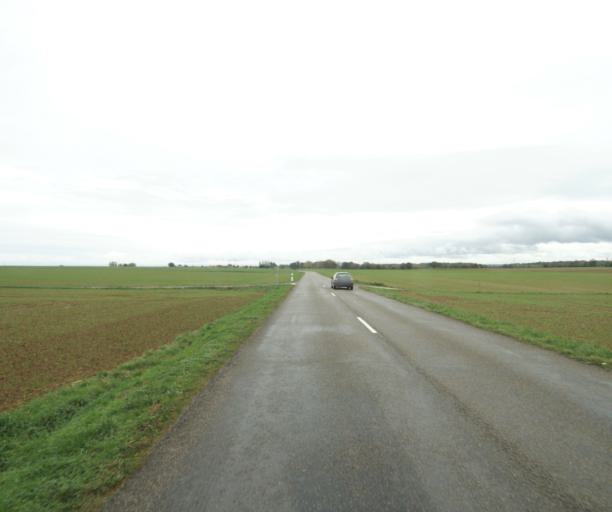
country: FR
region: Bourgogne
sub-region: Departement de Saone-et-Loire
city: Saint-Martin-Belle-Roche
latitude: 46.4671
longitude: 4.8595
